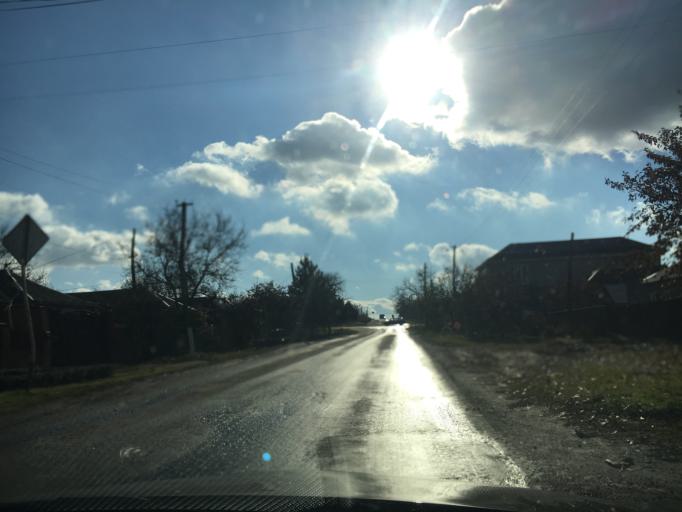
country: RU
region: Rostov
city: Matveyev Kurgan
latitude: 47.5606
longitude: 38.8682
